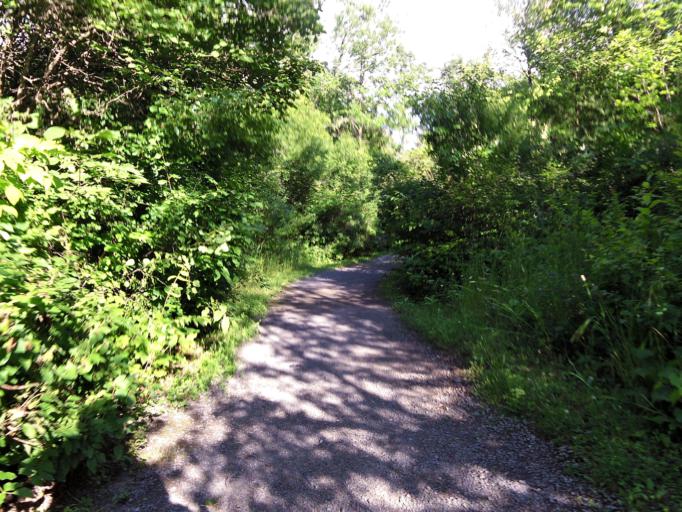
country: CA
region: Ontario
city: Bells Corners
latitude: 45.3469
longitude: -75.8555
